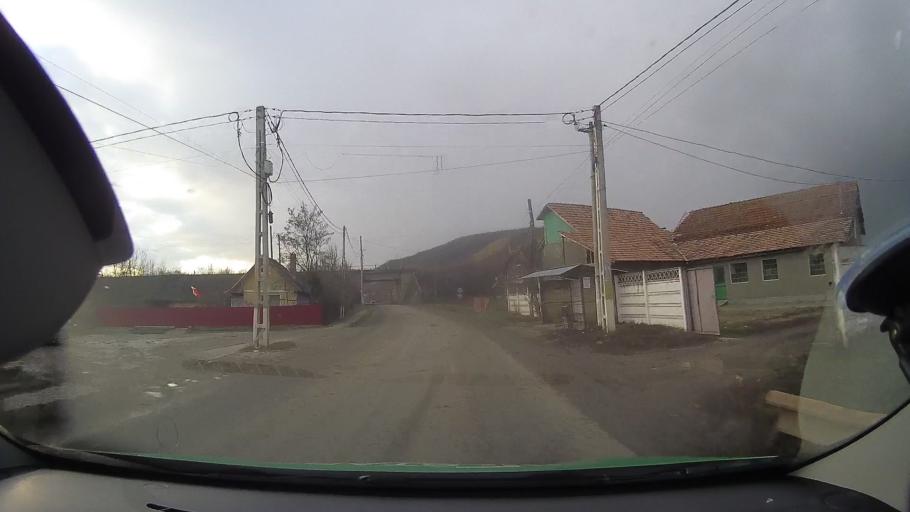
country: RO
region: Alba
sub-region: Comuna Lunca Muresului
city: Lunca Muresului
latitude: 46.4289
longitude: 23.9021
